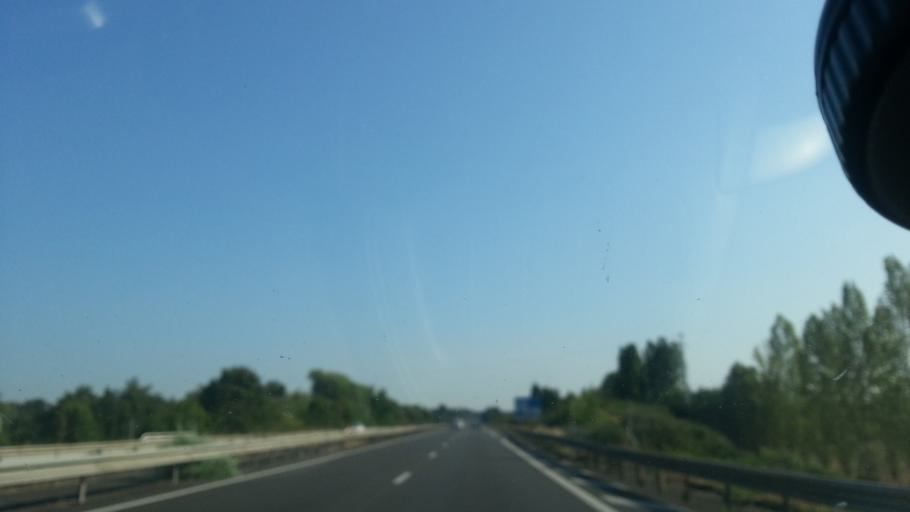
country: FR
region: Centre
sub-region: Departement d'Indre-et-Loire
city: La Celle-Saint-Avant
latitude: 47.0187
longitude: 0.5632
